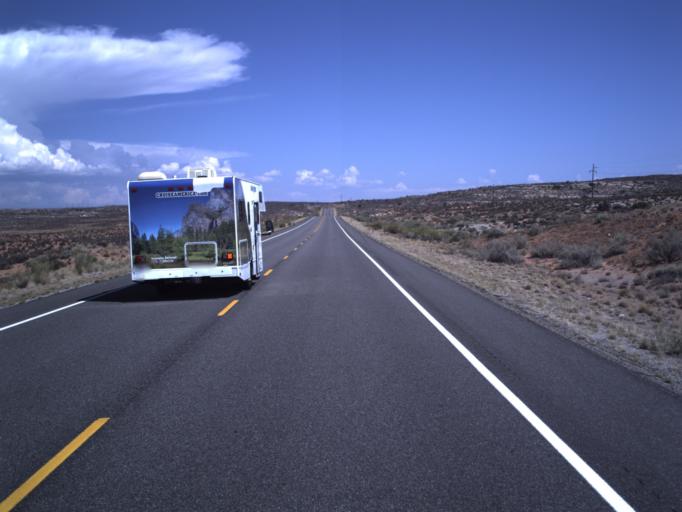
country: US
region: Utah
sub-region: San Juan County
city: Blanding
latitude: 37.3578
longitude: -109.5156
